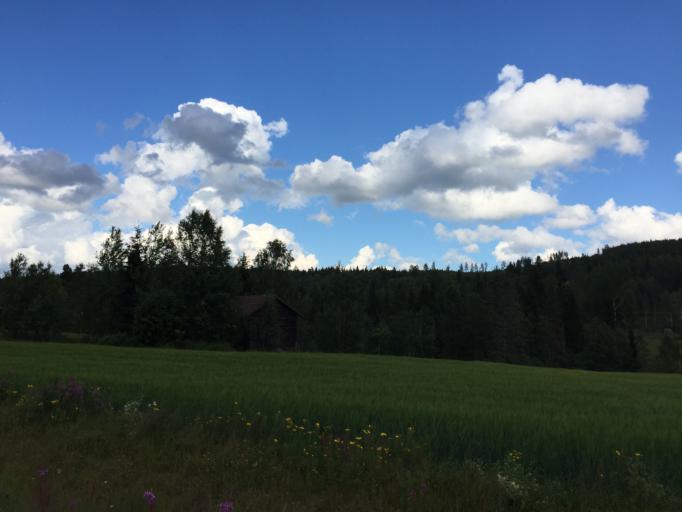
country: SE
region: Gaevleborg
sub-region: Ljusdals Kommun
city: Jaervsoe
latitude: 61.7163
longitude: 16.2943
